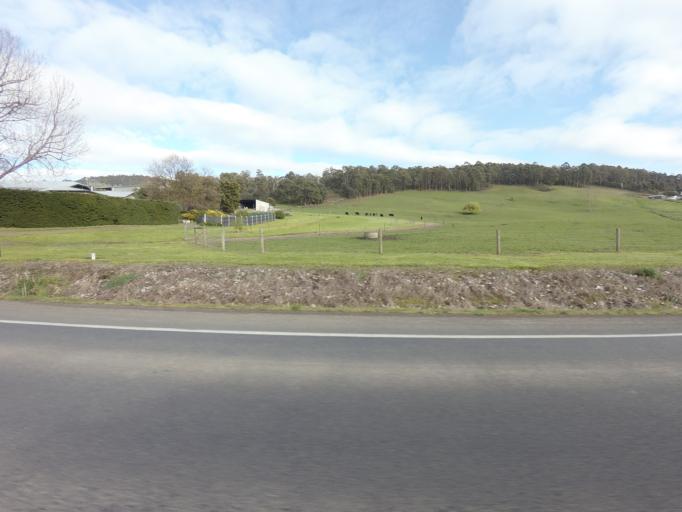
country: AU
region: Tasmania
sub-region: Huon Valley
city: Huonville
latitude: -43.0430
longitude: 147.0441
